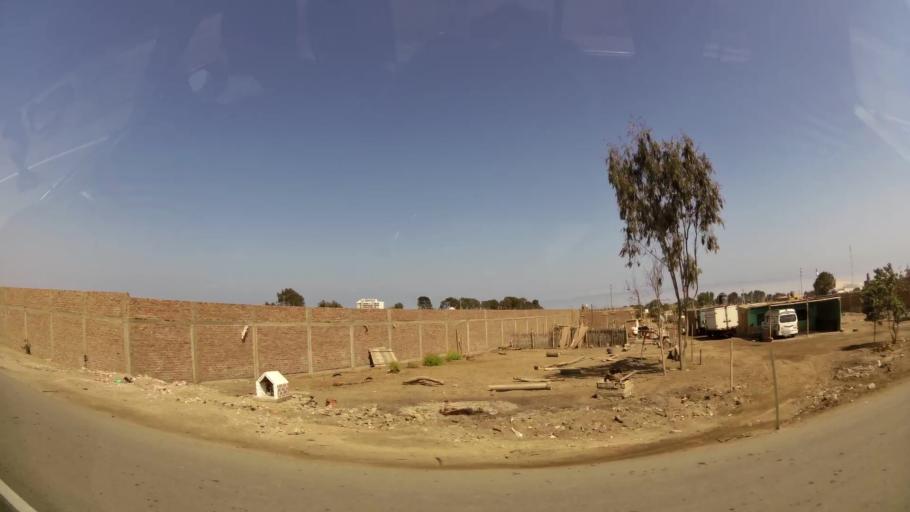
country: PE
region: Lima
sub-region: Provincia de Canete
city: Asia
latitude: -12.7819
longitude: -76.5806
